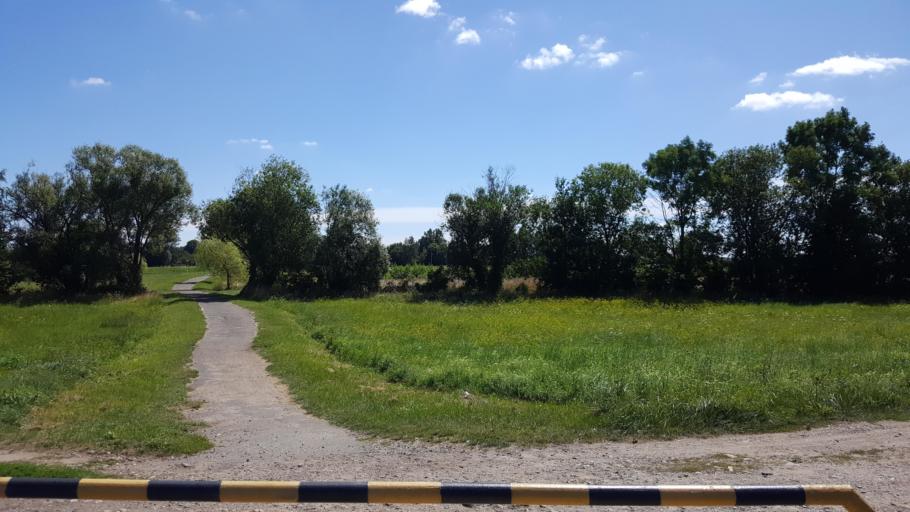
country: BY
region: Brest
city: Kobryn
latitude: 52.3405
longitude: 24.2369
